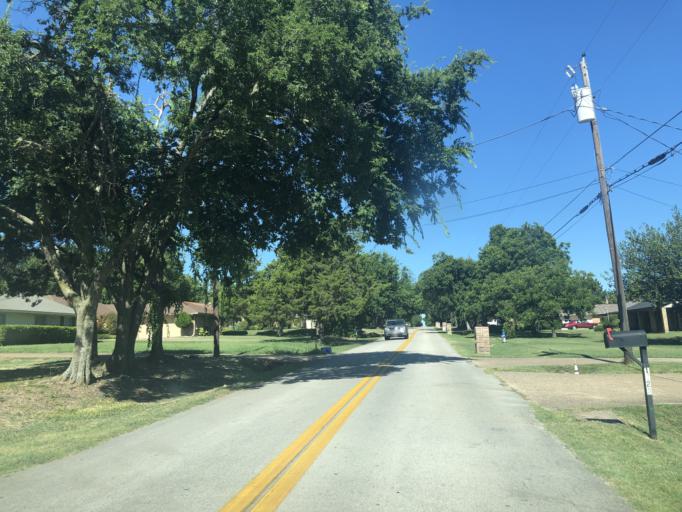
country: US
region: Texas
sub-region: Dallas County
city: Duncanville
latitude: 32.6561
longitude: -96.9373
